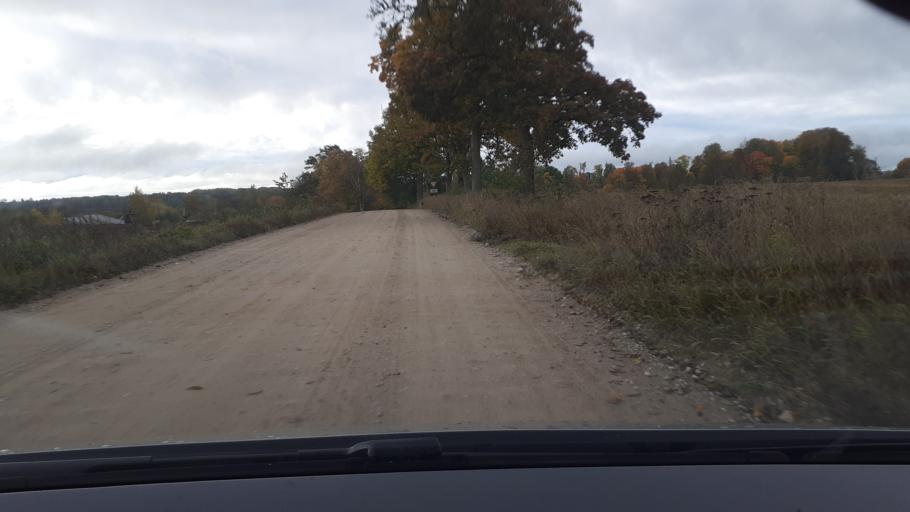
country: LV
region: Kuldigas Rajons
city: Kuldiga
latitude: 57.0226
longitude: 21.9136
